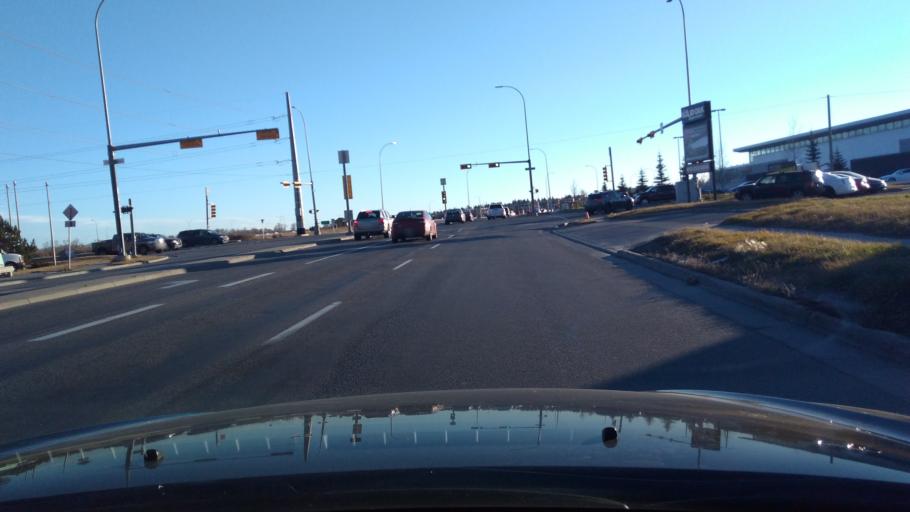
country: CA
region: Alberta
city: Calgary
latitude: 50.9879
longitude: -114.0398
